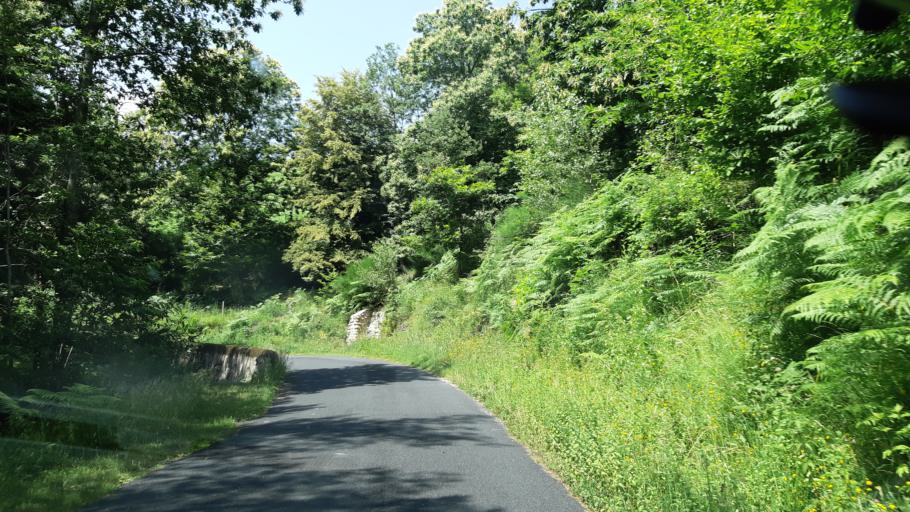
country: FR
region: Languedoc-Roussillon
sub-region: Departement des Pyrenees-Orientales
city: Arles
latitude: 42.5394
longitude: 2.5697
